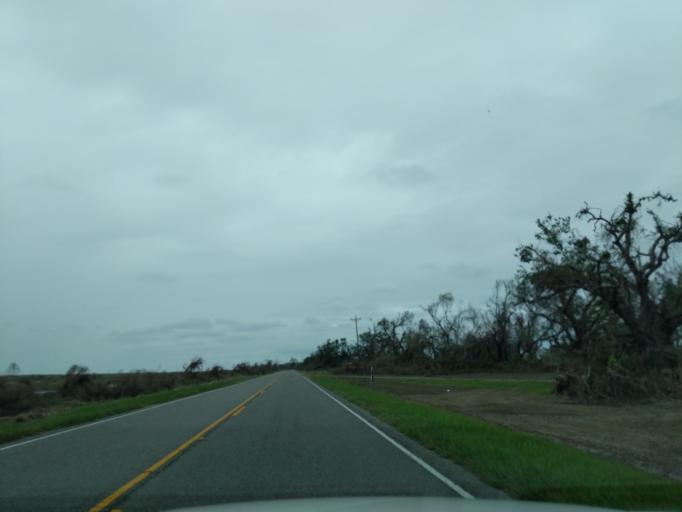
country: US
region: Louisiana
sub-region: Cameron Parish
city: Cameron
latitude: 29.7861
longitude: -93.1189
